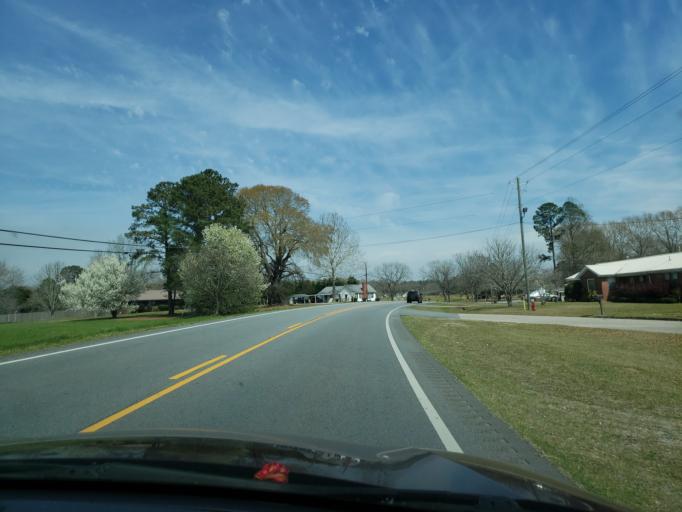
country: US
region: Alabama
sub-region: Elmore County
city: Tallassee
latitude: 32.5568
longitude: -85.8273
